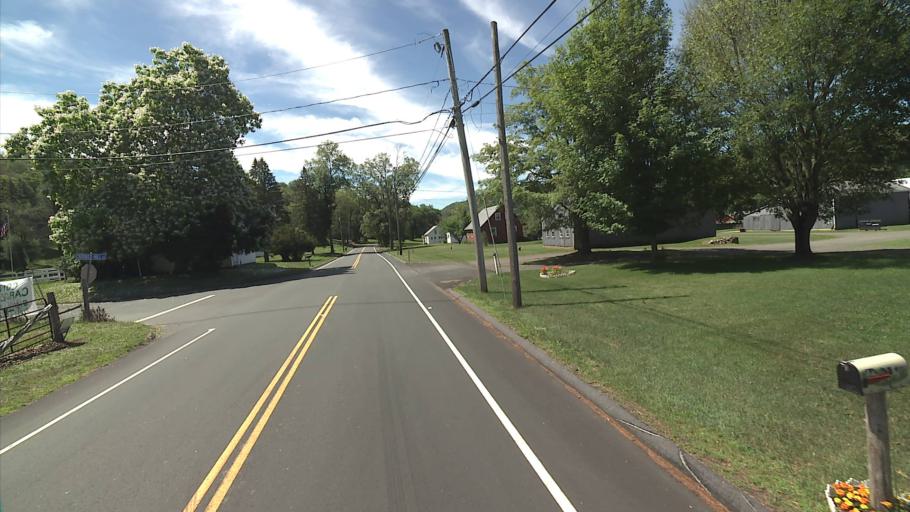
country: US
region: Connecticut
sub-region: Middlesex County
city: Durham
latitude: 41.4342
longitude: -72.6904
